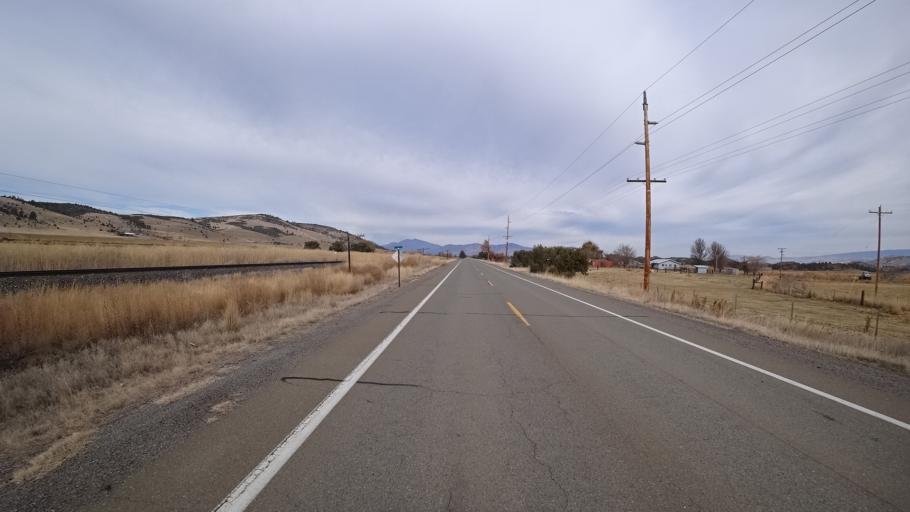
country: US
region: California
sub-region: Siskiyou County
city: Montague
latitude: 41.6604
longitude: -122.5206
